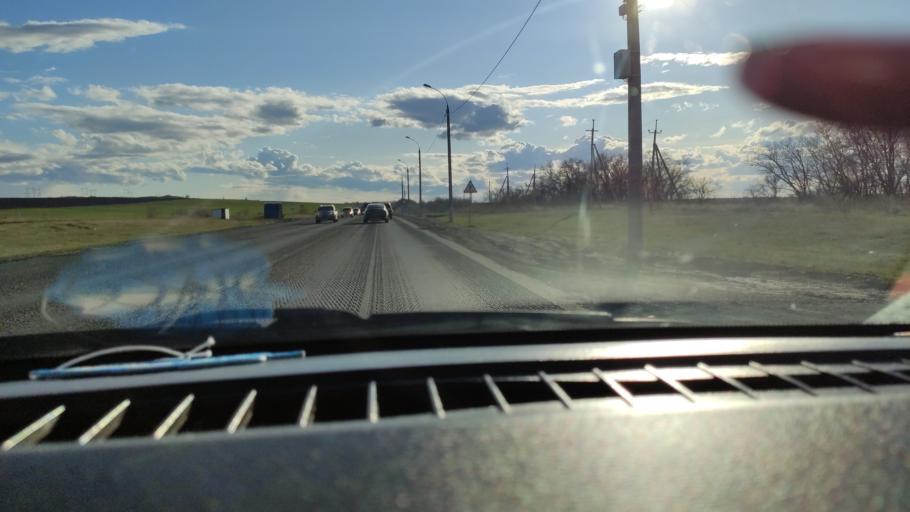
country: RU
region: Saratov
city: Shumeyka
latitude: 51.7897
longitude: 46.1492
